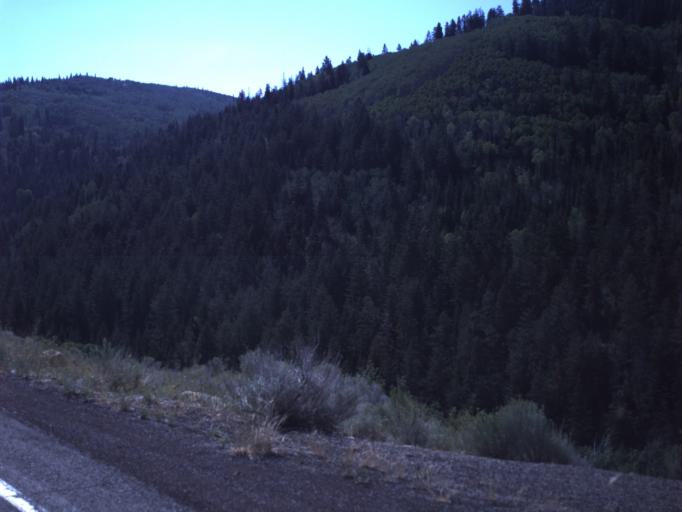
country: US
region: Utah
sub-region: Sanpete County
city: Fairview
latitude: 39.6479
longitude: -111.3796
